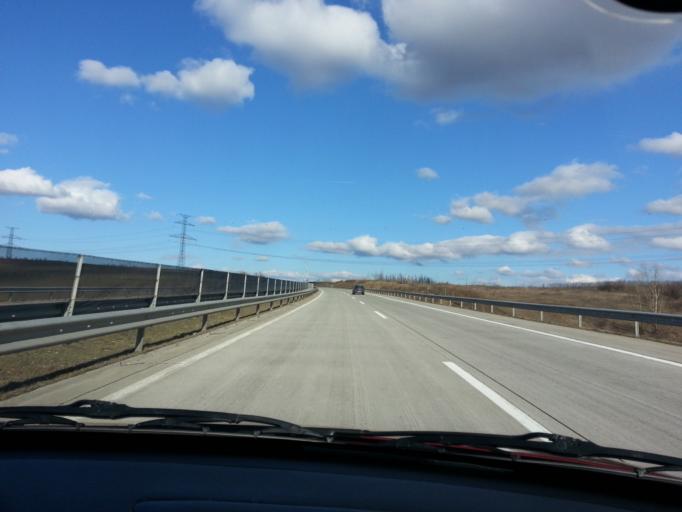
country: HU
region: Pest
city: Nagytarcsa
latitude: 47.5454
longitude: 19.3121
